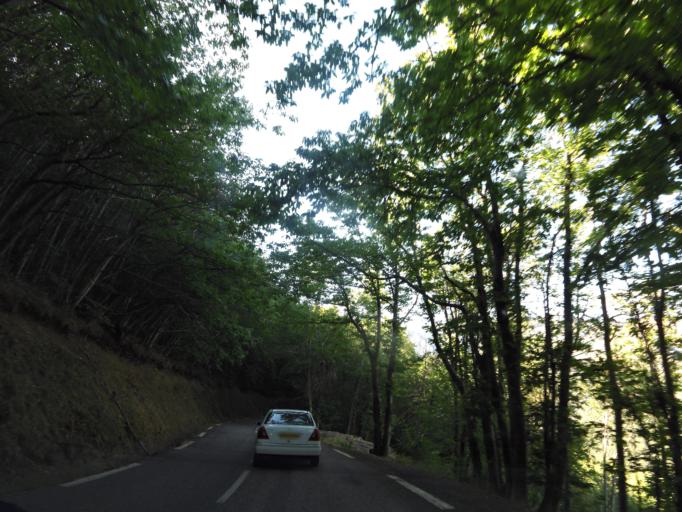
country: FR
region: Languedoc-Roussillon
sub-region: Departement du Gard
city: Valleraugue
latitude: 44.0847
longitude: 3.5816
